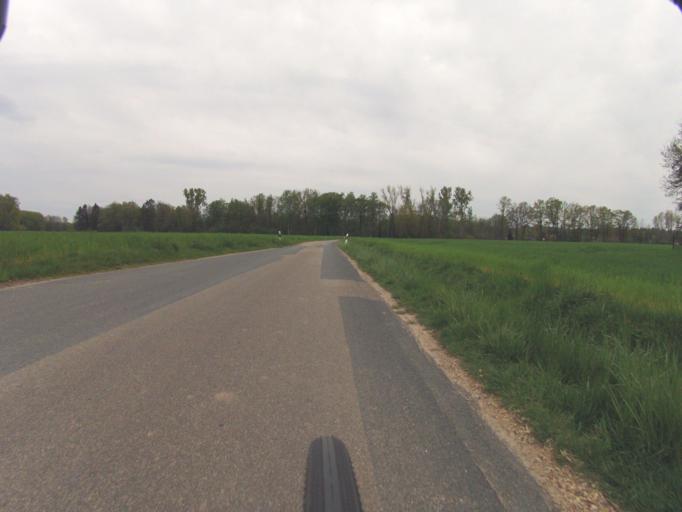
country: DE
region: North Rhine-Westphalia
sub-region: Regierungsbezirk Munster
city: Mettingen
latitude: 52.3155
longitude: 7.8237
